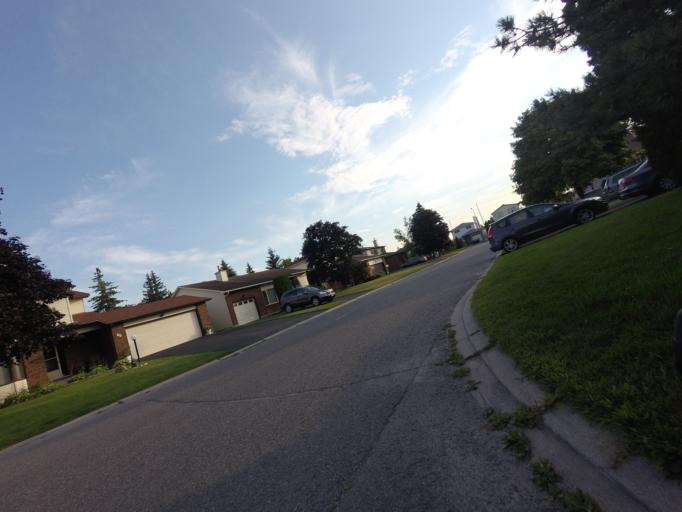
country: CA
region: Ontario
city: Bells Corners
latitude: 45.2776
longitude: -75.7772
